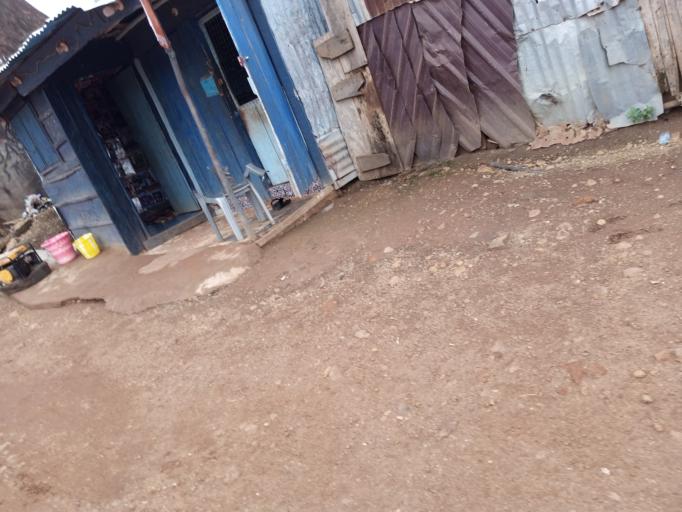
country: SL
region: Western Area
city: Hastings
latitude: 8.3772
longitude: -13.1540
